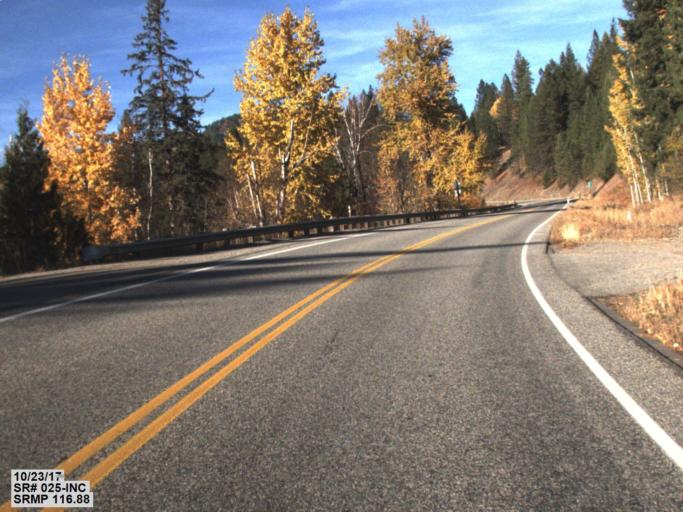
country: CA
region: British Columbia
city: Rossland
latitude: 48.9476
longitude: -117.7925
